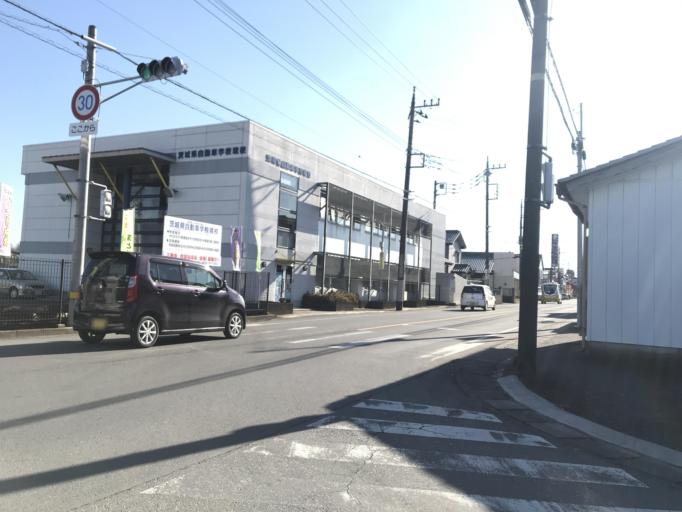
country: JP
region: Ibaraki
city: Sakai
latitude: 36.1206
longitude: 139.7985
